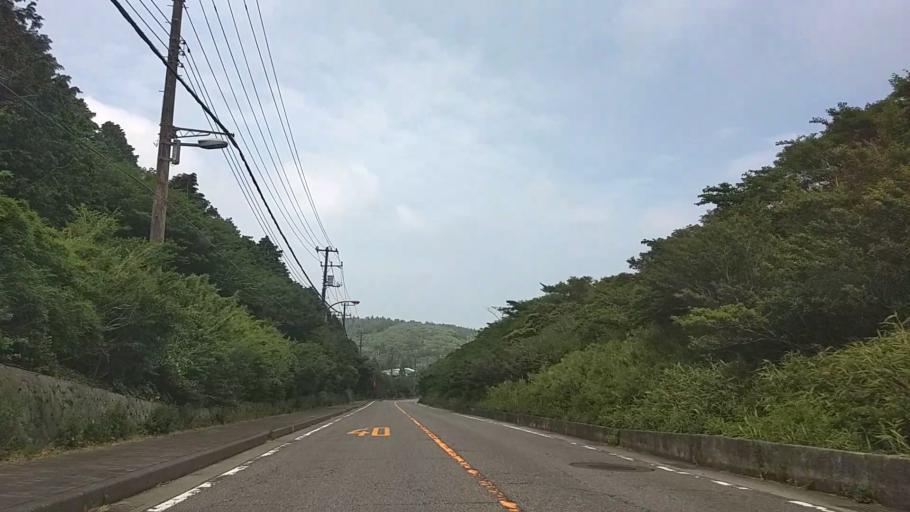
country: JP
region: Kanagawa
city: Hakone
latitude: 35.2179
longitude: 139.0392
